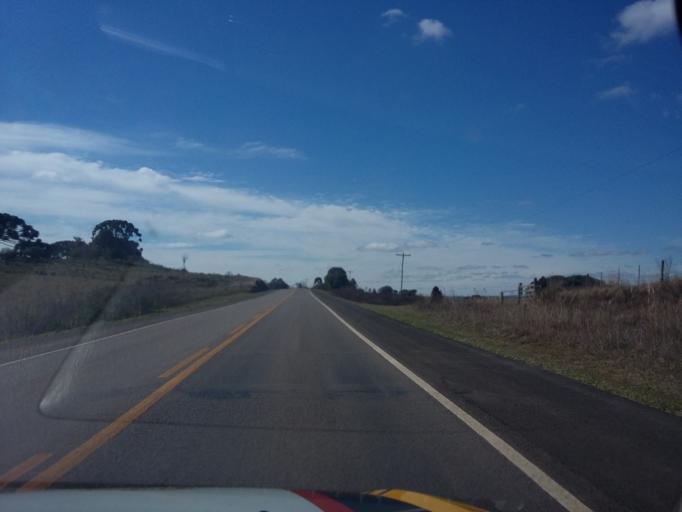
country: BR
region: Rio Grande do Sul
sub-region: Vacaria
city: Vacaria
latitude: -28.7112
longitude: -51.0839
